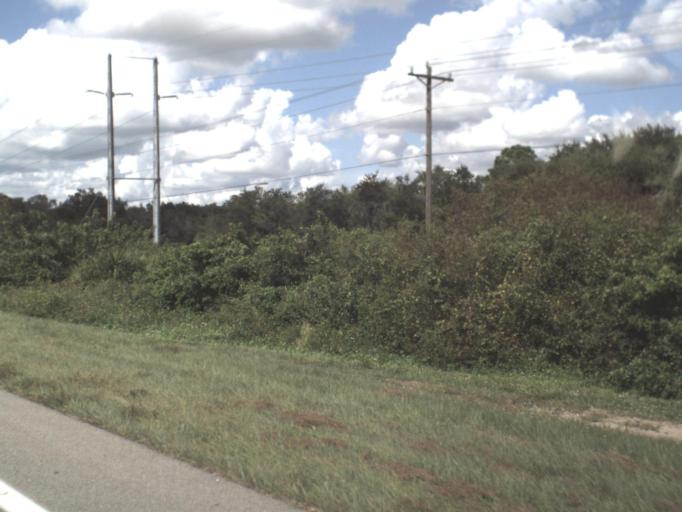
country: US
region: Florida
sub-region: Lee County
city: Lehigh Acres
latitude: 26.5609
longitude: -81.6656
